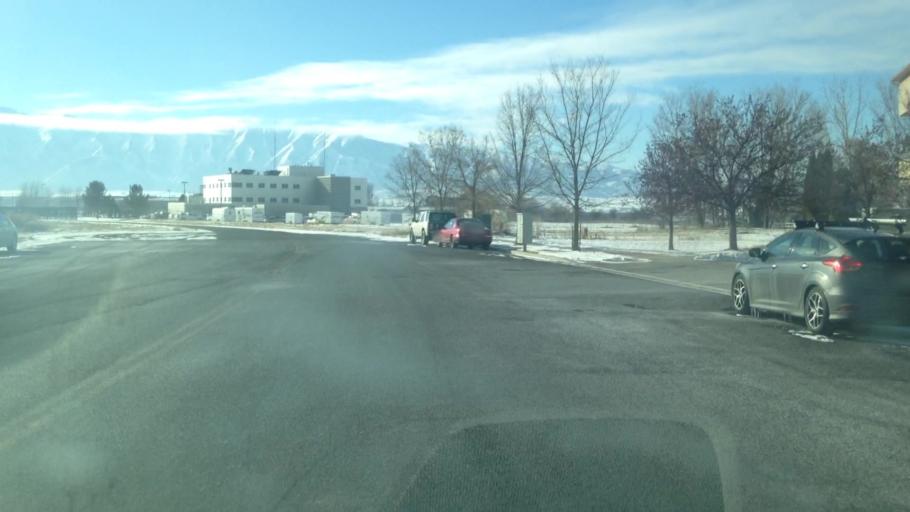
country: US
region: Utah
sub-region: Cache County
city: Logan
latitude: 41.7384
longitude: -111.8622
